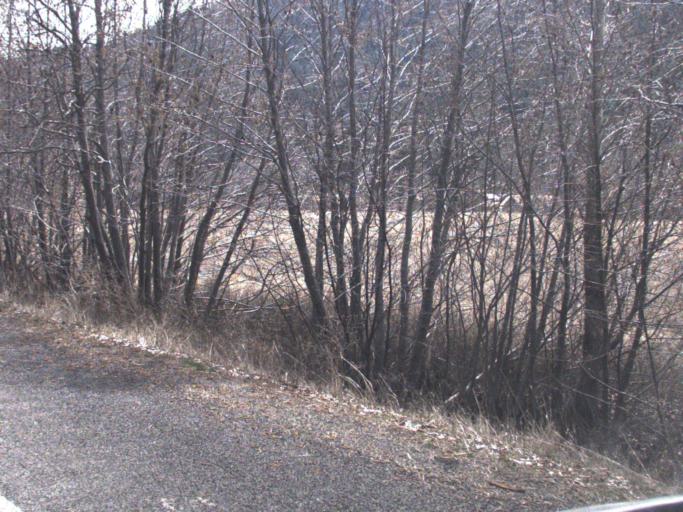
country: US
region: Washington
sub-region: Kittitas County
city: Cle Elum
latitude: 46.9169
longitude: -121.0415
